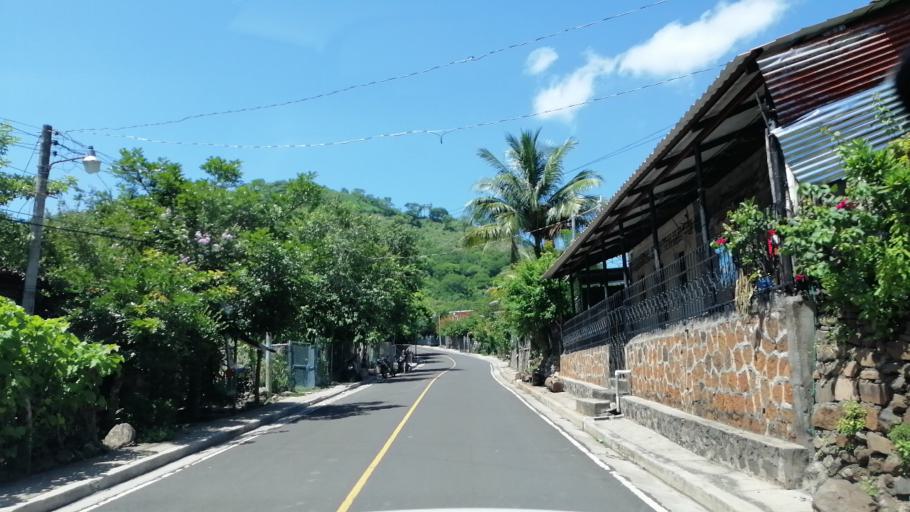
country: SV
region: San Miguel
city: Sesori
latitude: 13.8089
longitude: -88.4022
